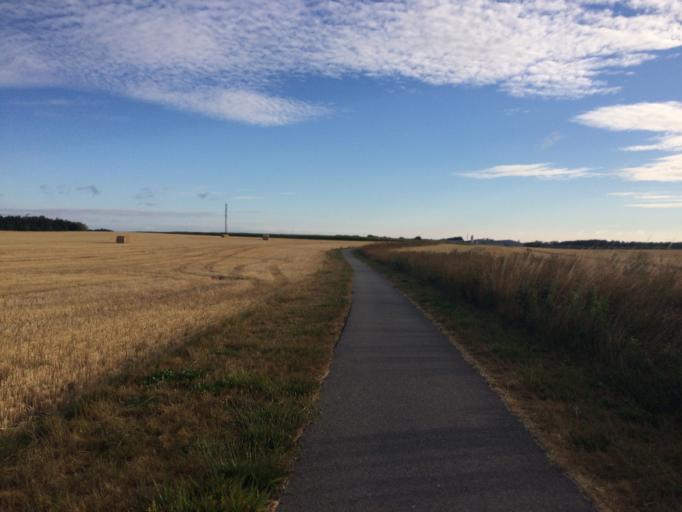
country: DK
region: Central Jutland
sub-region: Holstebro Kommune
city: Vinderup
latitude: 56.6066
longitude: 8.8689
